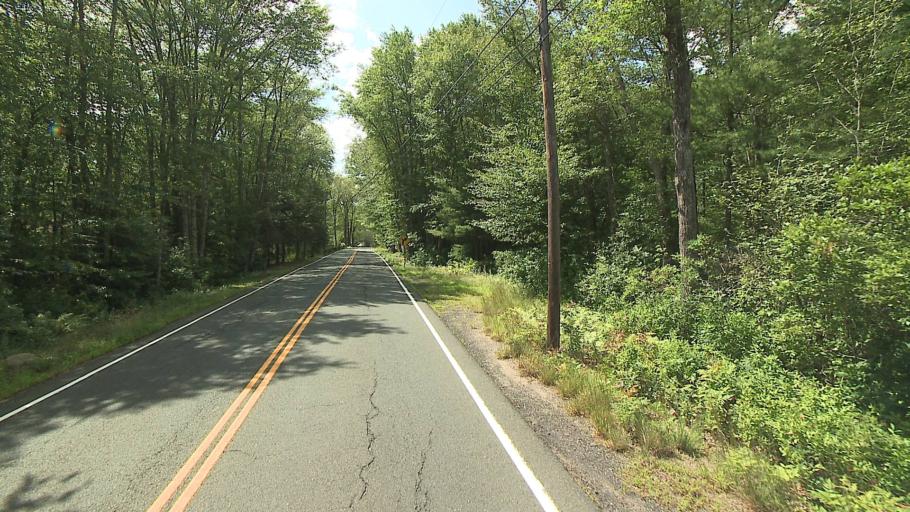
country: US
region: Connecticut
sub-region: Tolland County
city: Crystal Lake
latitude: 41.9335
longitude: -72.3522
